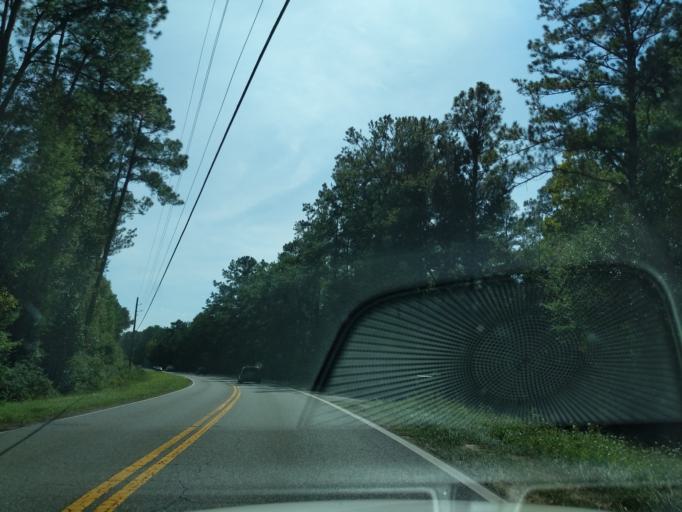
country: US
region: Florida
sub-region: Okaloosa County
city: Crestview
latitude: 30.7408
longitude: -86.6230
